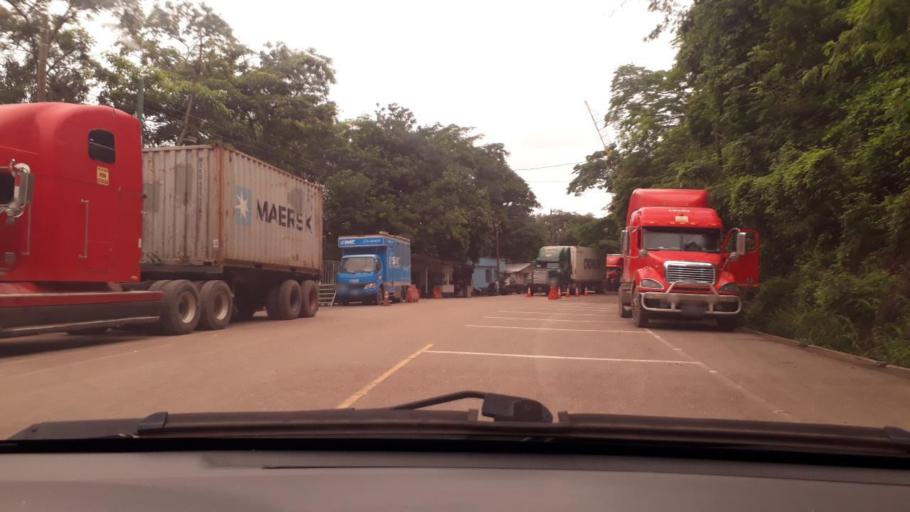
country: SV
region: Santa Ana
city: Metapan
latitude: 14.4134
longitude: -89.4382
